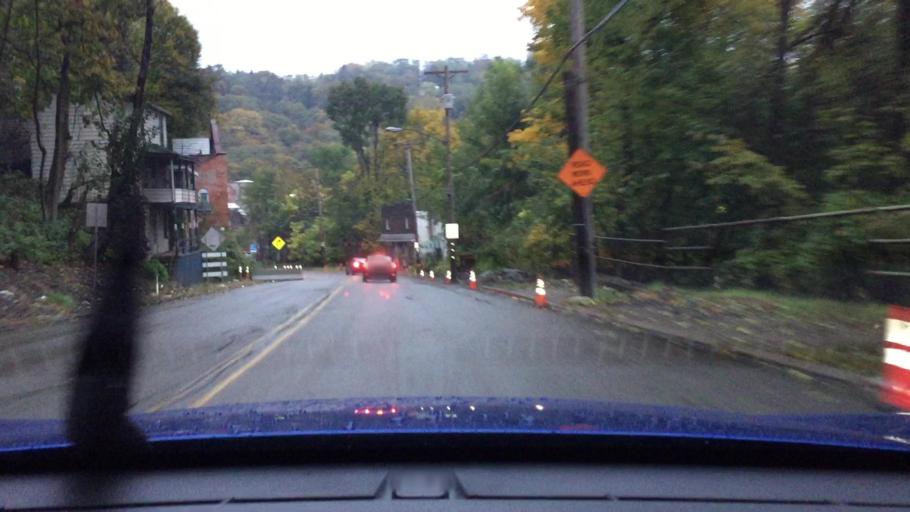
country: US
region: Pennsylvania
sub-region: Allegheny County
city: Green Tree
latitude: 40.4390
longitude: -80.0352
